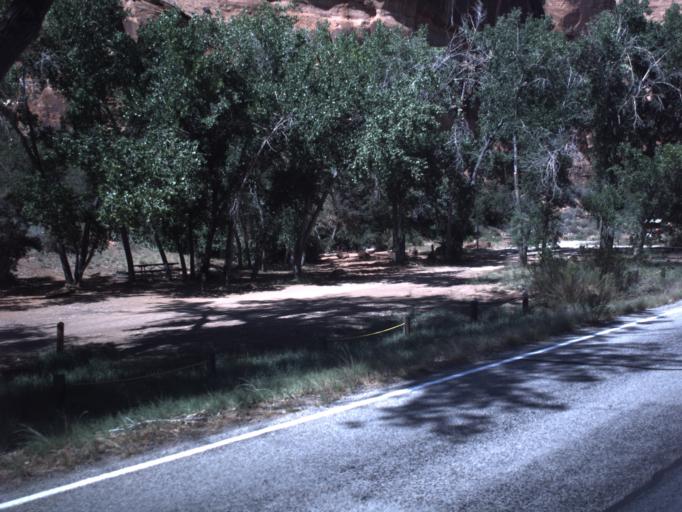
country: US
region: Utah
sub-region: Grand County
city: Moab
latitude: 38.5378
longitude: -109.6040
